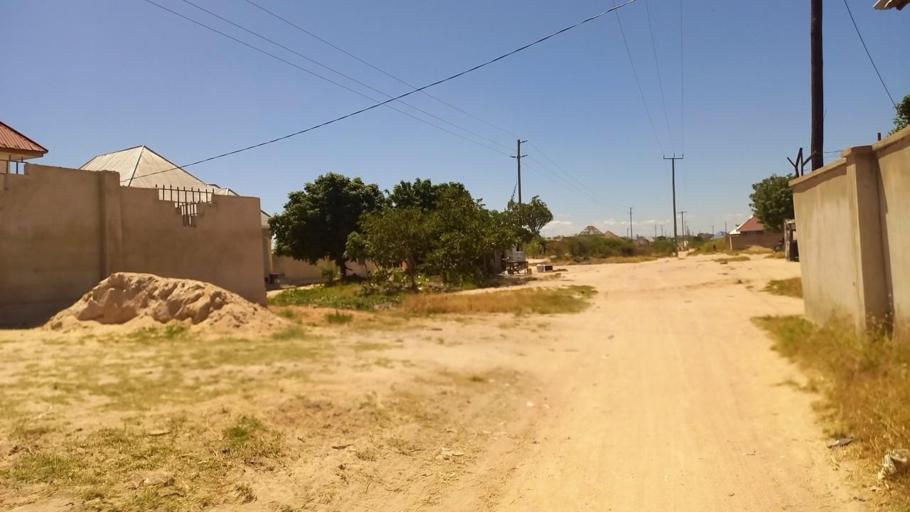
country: TZ
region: Dodoma
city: Dodoma
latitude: -6.1337
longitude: 35.7163
